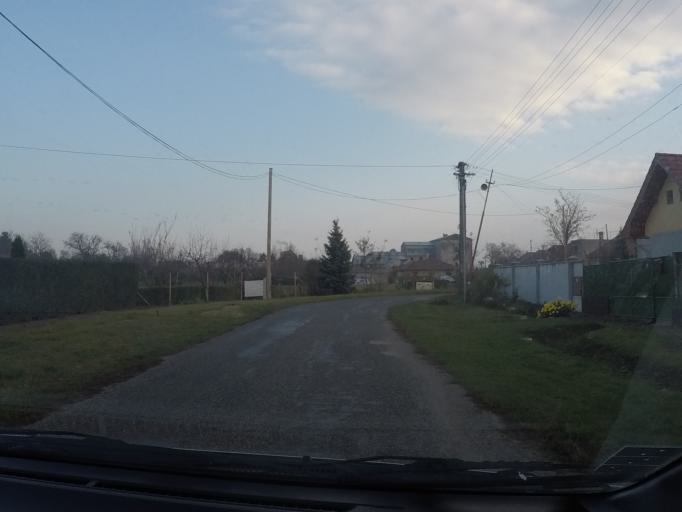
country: SK
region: Nitriansky
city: Zeliezovce
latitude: 48.0943
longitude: 18.5407
